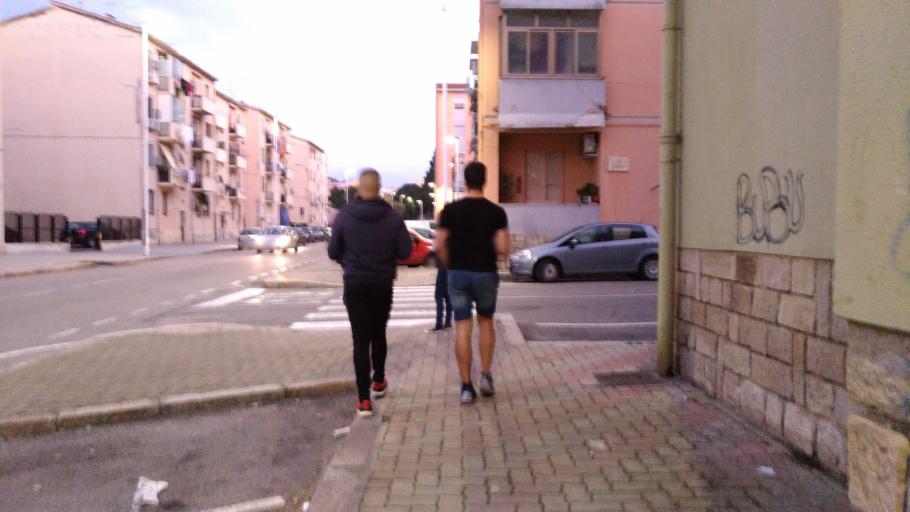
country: IT
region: Sardinia
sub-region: Provincia di Cagliari
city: Su Planu
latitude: 39.2401
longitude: 9.1024
